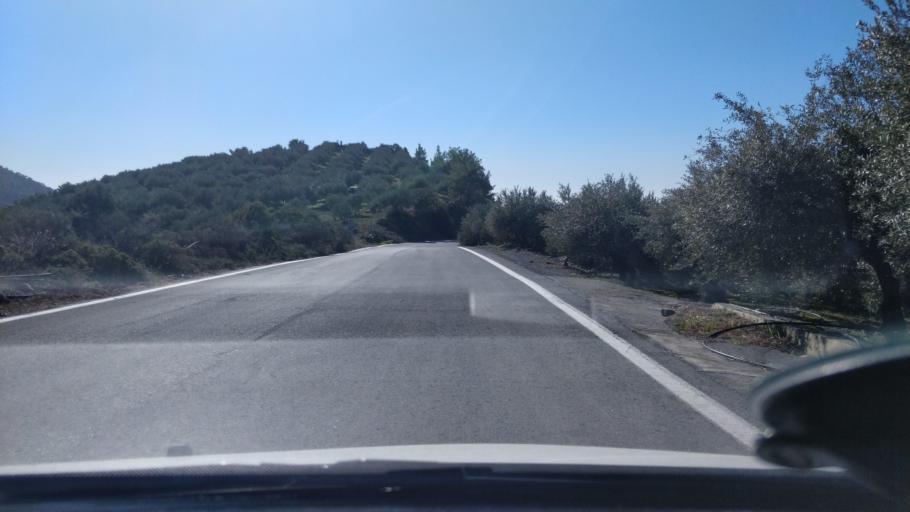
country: GR
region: Crete
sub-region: Nomos Irakleiou
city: Kastelli
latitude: 35.0282
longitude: 25.4494
